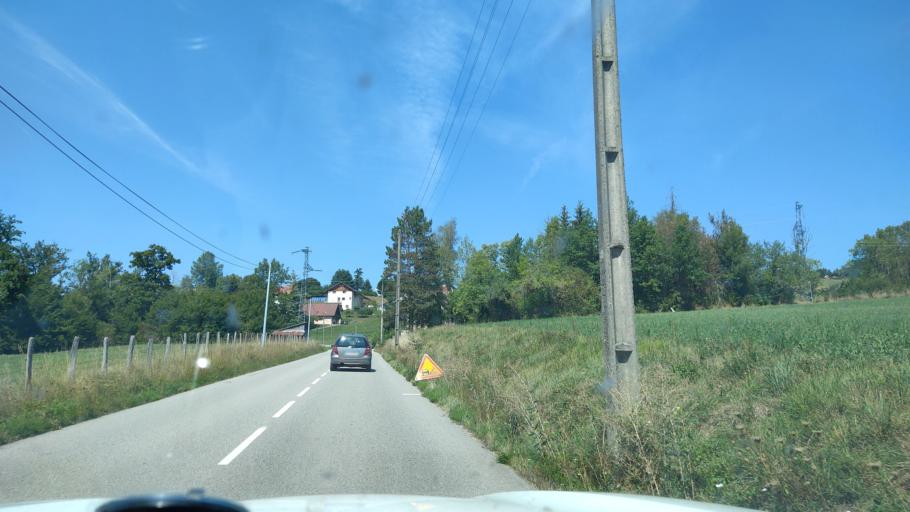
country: FR
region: Rhone-Alpes
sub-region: Departement de la Savoie
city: Novalaise
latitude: 45.5981
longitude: 5.7673
